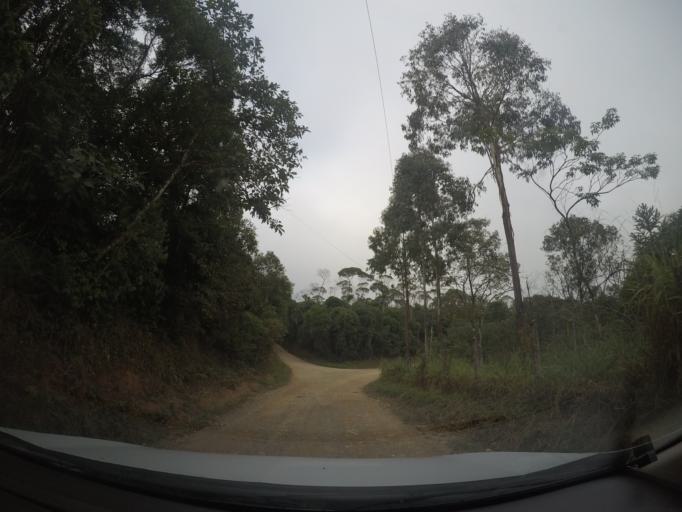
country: BR
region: Parana
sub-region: Colombo
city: Colombo
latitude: -25.3171
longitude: -49.2479
